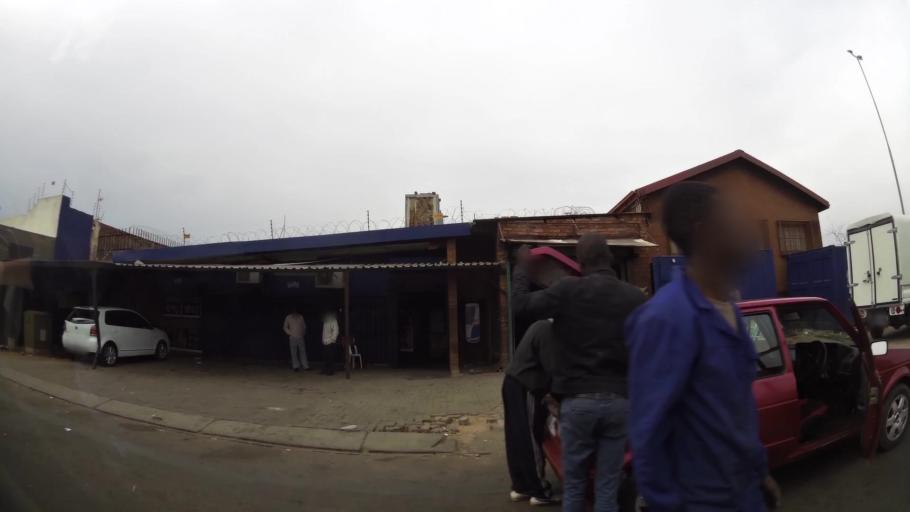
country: ZA
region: Gauteng
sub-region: City of Tshwane Metropolitan Municipality
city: Pretoria
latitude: -25.7126
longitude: 28.3458
